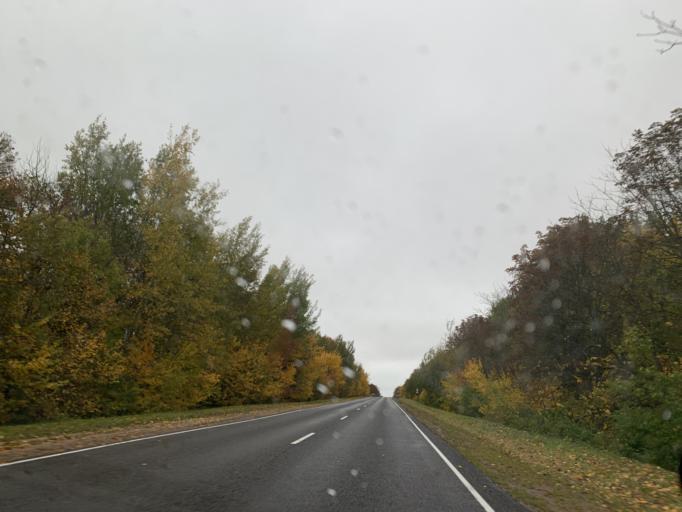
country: BY
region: Minsk
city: Haradzyeya
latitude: 53.3878
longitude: 26.5700
